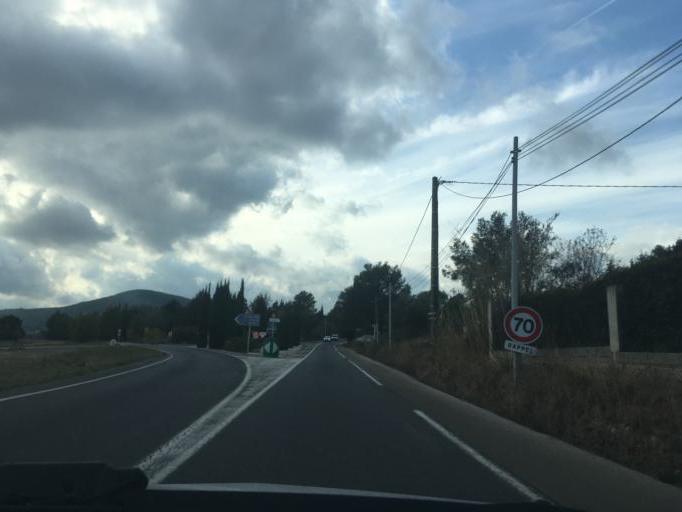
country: FR
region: Provence-Alpes-Cote d'Azur
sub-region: Departement du Var
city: Cuers
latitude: 43.2454
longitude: 6.0879
